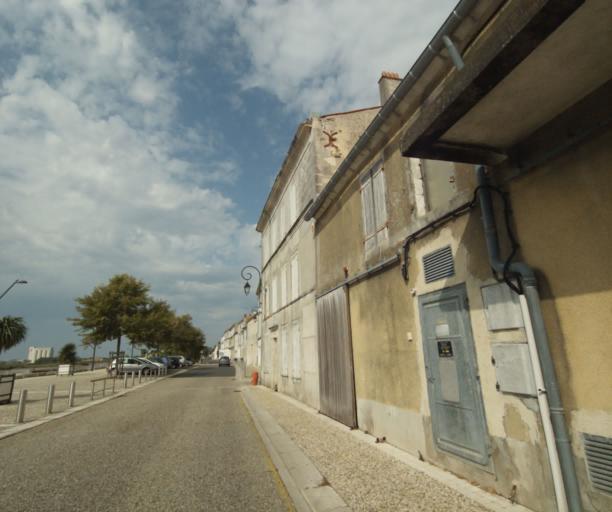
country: FR
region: Poitou-Charentes
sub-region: Departement de la Charente-Maritime
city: Tonnay-Charente
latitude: 45.9424
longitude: -0.8905
